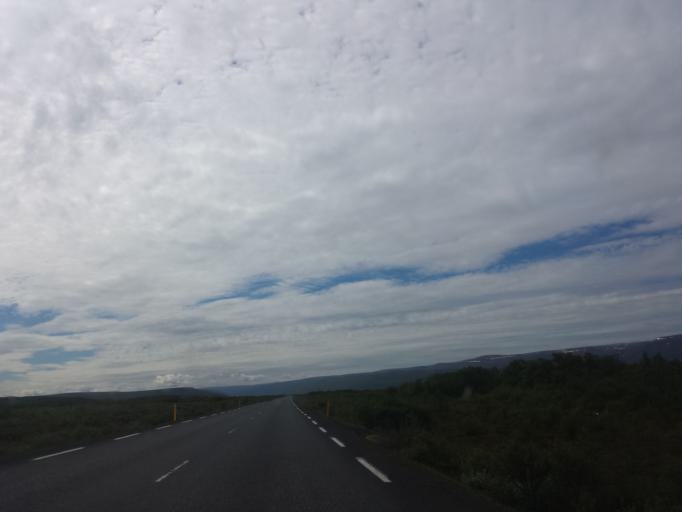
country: IS
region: Northeast
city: Husavik
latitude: 65.9459
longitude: -17.4344
